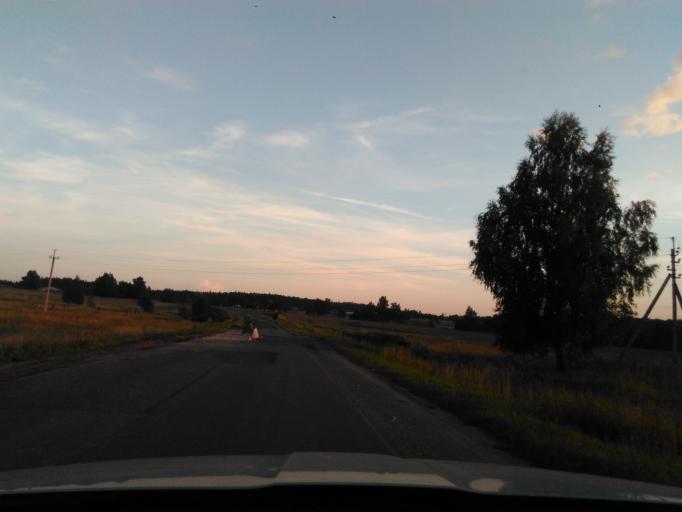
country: RU
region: Moskovskaya
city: Klin
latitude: 56.1880
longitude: 36.8108
